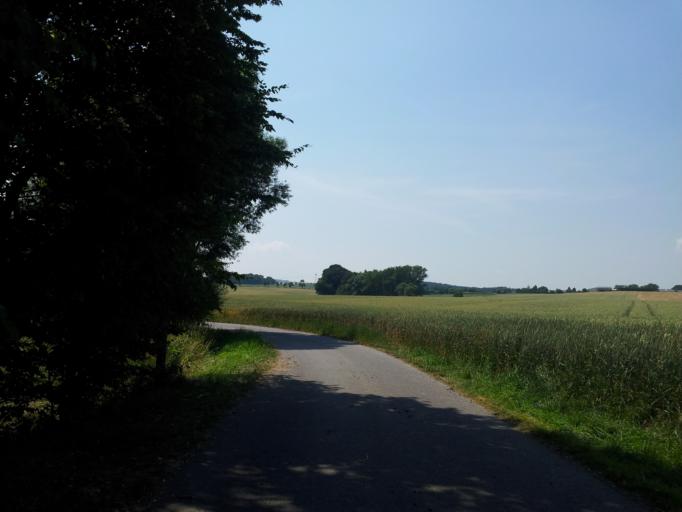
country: DE
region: Saxony
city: Burkau
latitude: 51.2055
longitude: 14.1969
